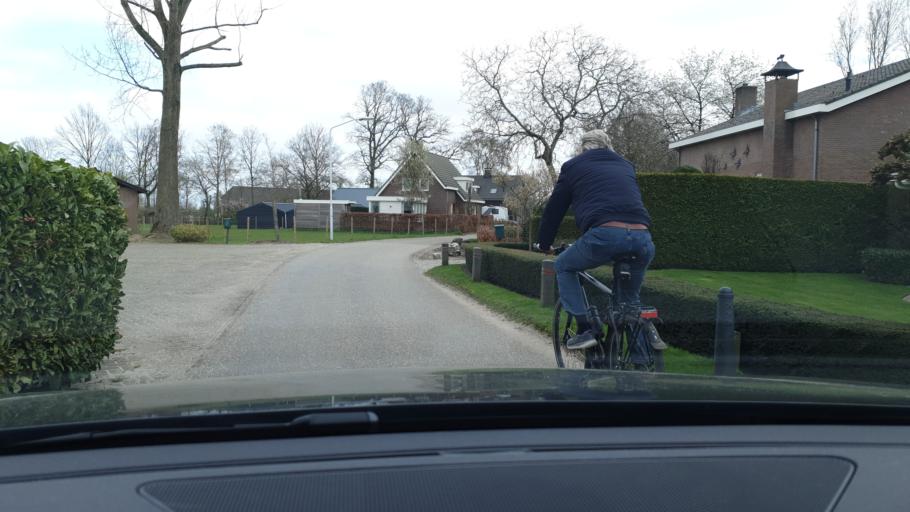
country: NL
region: North Brabant
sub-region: Gemeente Best
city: Best
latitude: 51.5126
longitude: 5.3612
